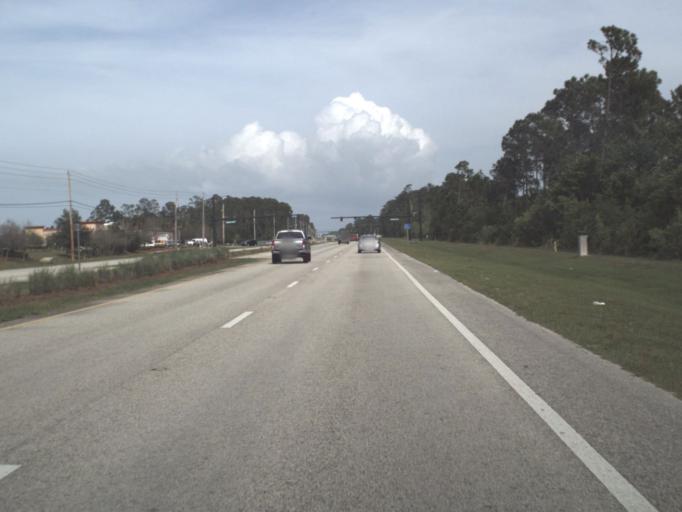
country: US
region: Florida
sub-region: Flagler County
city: Bunnell
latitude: 29.4754
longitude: -81.2170
